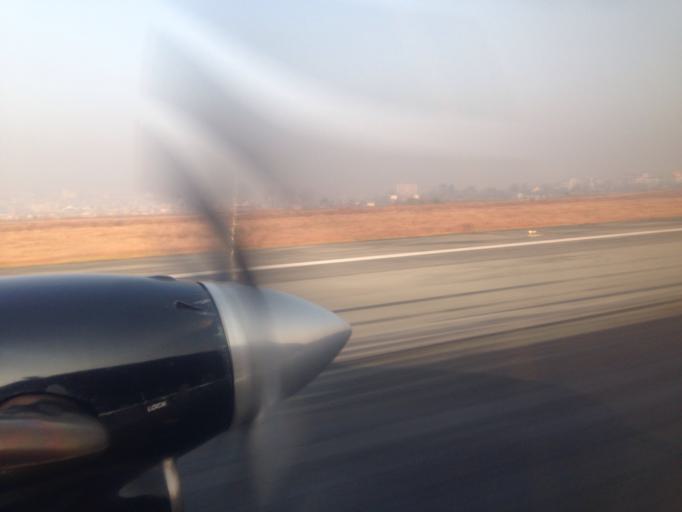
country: NP
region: Central Region
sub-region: Bagmati Zone
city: Kathmandu
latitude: 27.6862
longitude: 85.3544
